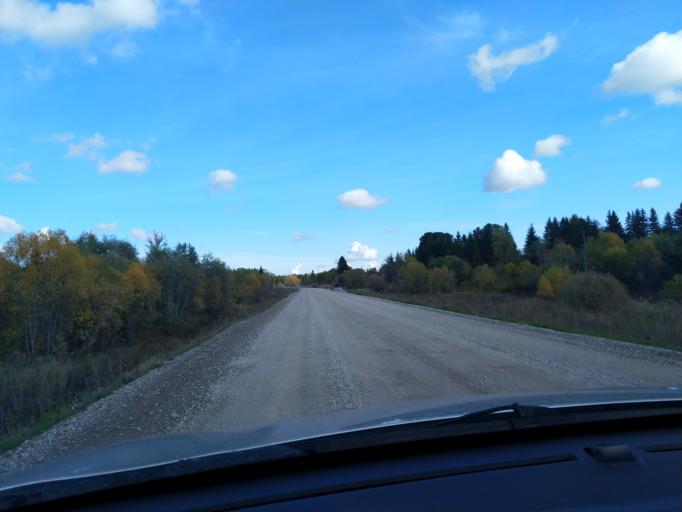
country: RU
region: Perm
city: Usol'ye
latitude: 59.4612
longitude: 56.3591
